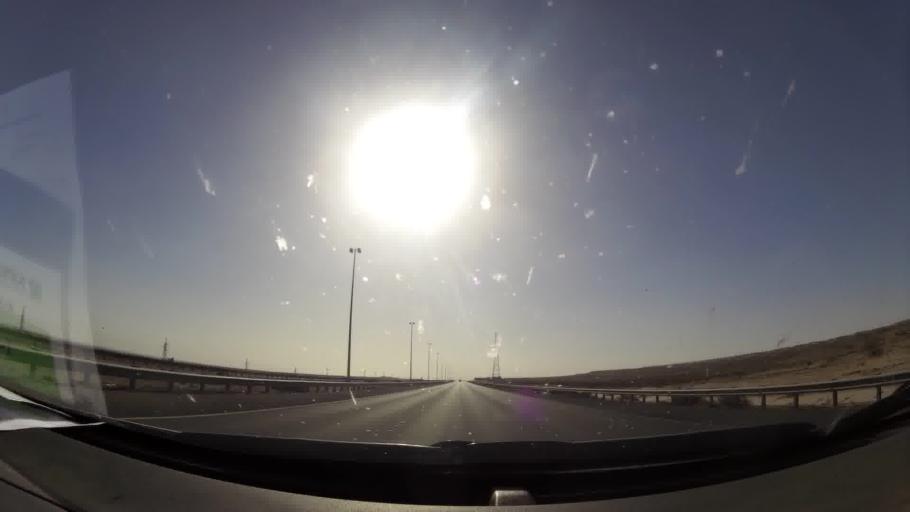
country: KW
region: Al Asimah
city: Kuwait City
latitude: 29.5588
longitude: 47.8839
